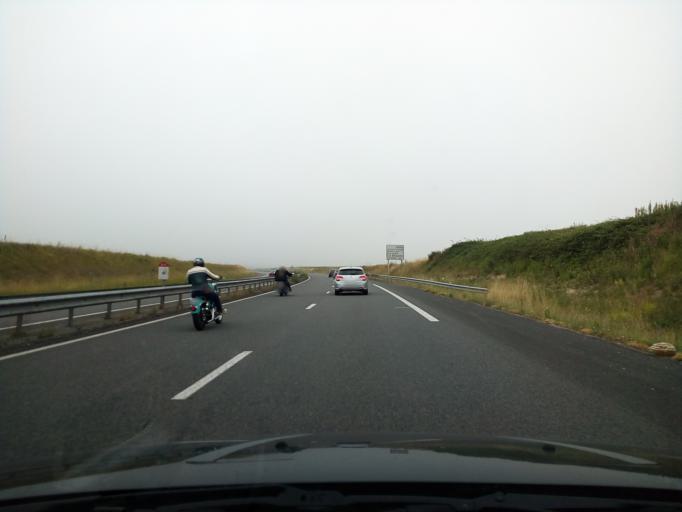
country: FR
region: Poitou-Charentes
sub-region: Departement de la Charente
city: Jarnac
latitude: 45.6981
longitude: -0.1245
